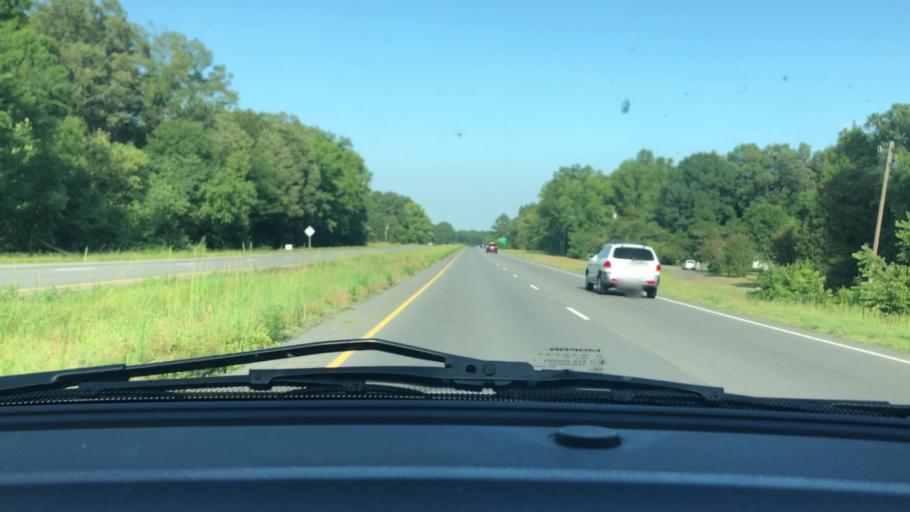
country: US
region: North Carolina
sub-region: Chatham County
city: Farmville
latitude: 35.5561
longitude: -79.2840
